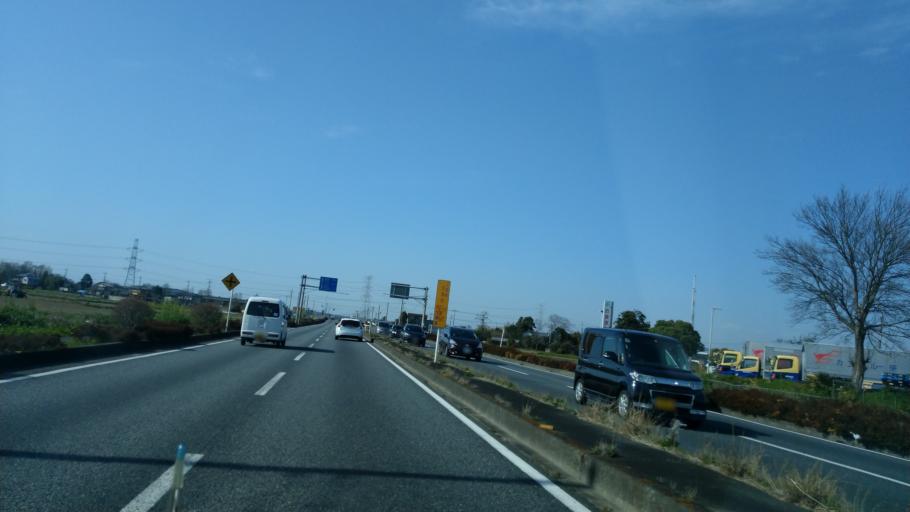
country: JP
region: Saitama
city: Sakado
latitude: 35.9966
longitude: 139.4537
